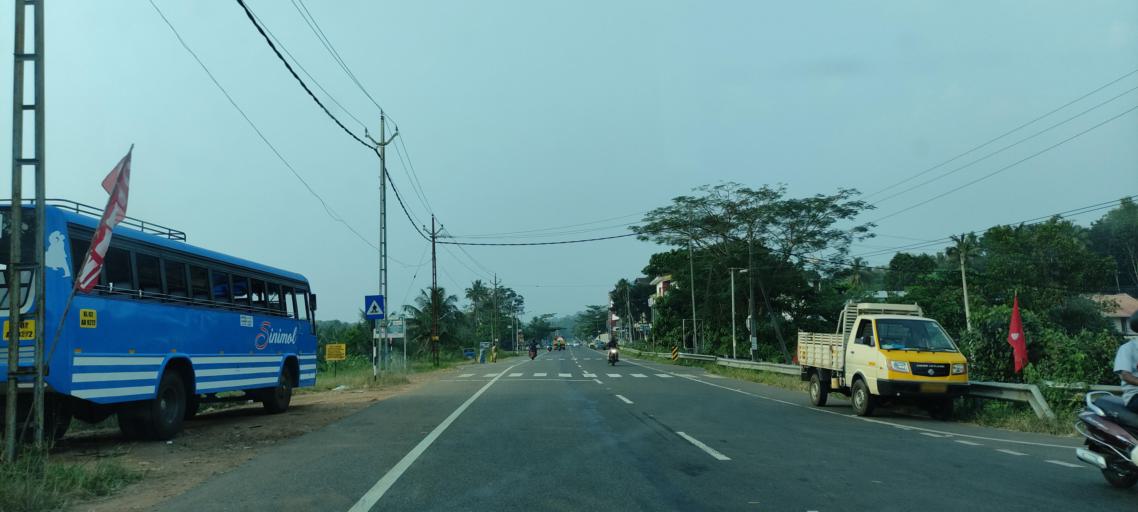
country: IN
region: Kerala
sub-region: Pattanamtitta
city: Adur
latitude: 9.0916
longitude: 76.7535
